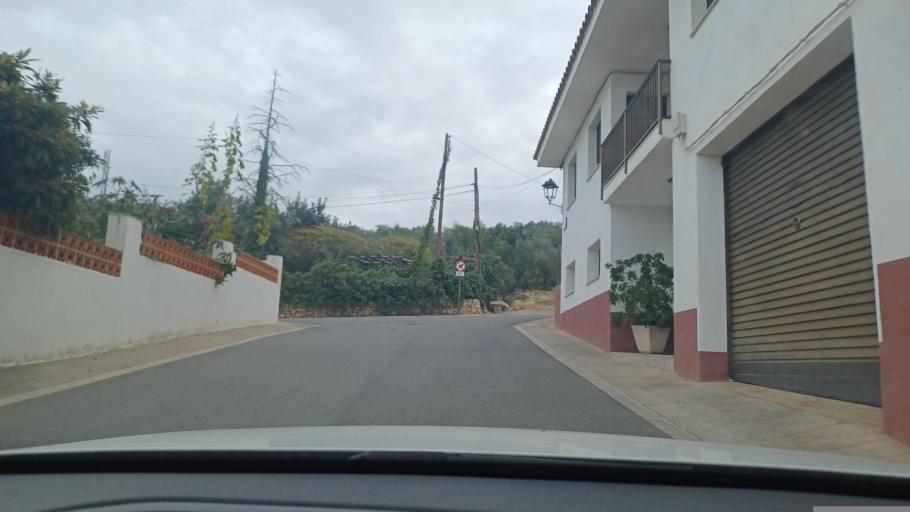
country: ES
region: Catalonia
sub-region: Provincia de Tarragona
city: Santa Barbara
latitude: 40.6567
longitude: 0.4700
